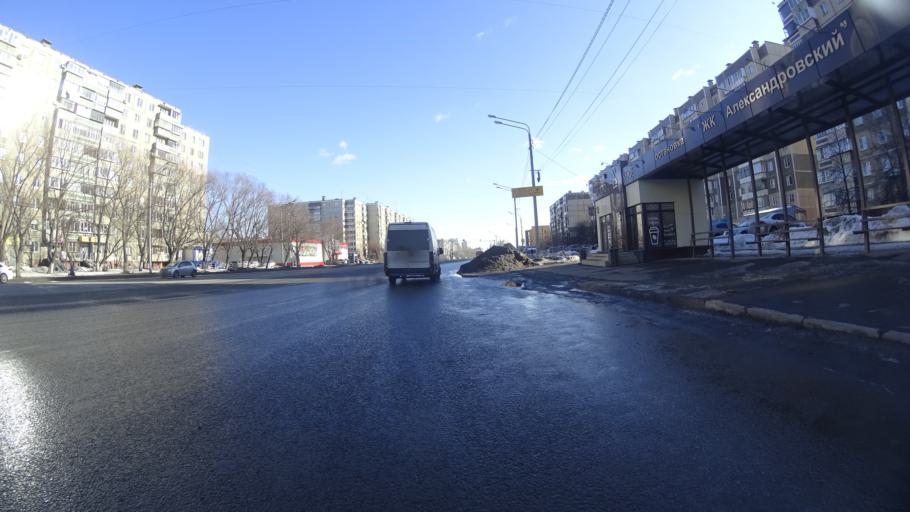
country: RU
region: Chelyabinsk
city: Roshchino
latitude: 55.1902
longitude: 61.2815
